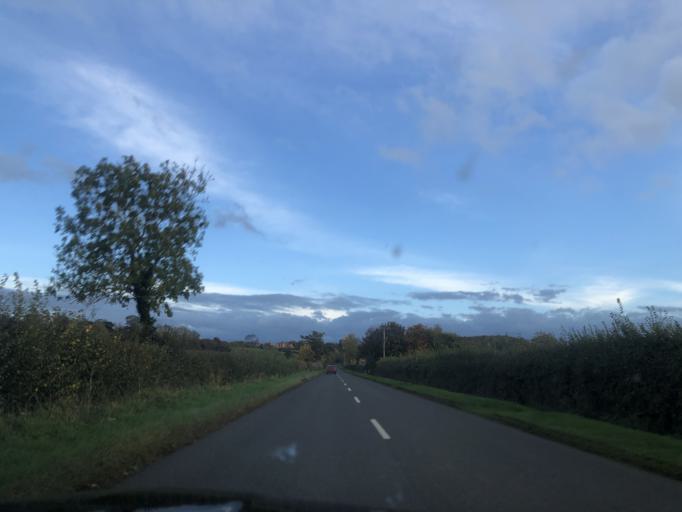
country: GB
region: England
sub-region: Warwickshire
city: Harbury
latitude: 52.2425
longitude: -1.4774
